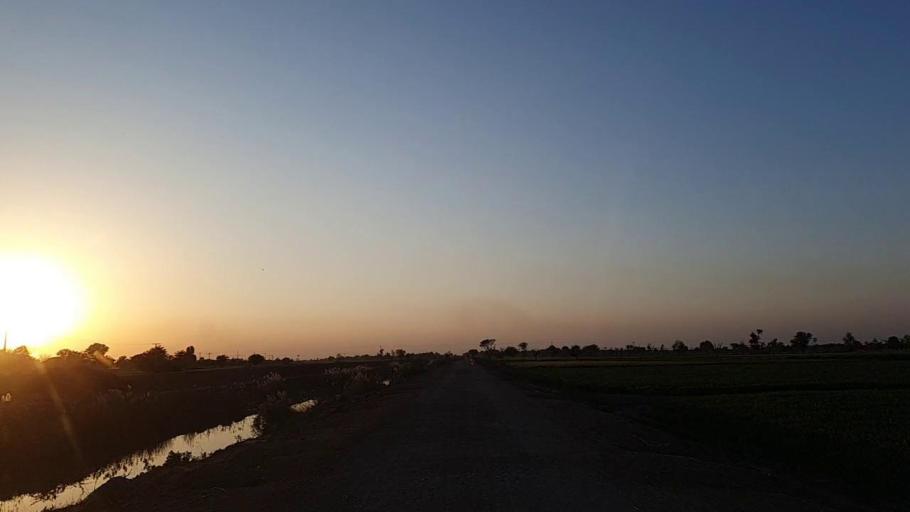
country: PK
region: Sindh
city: Jam Sahib
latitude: 26.3100
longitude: 68.6617
